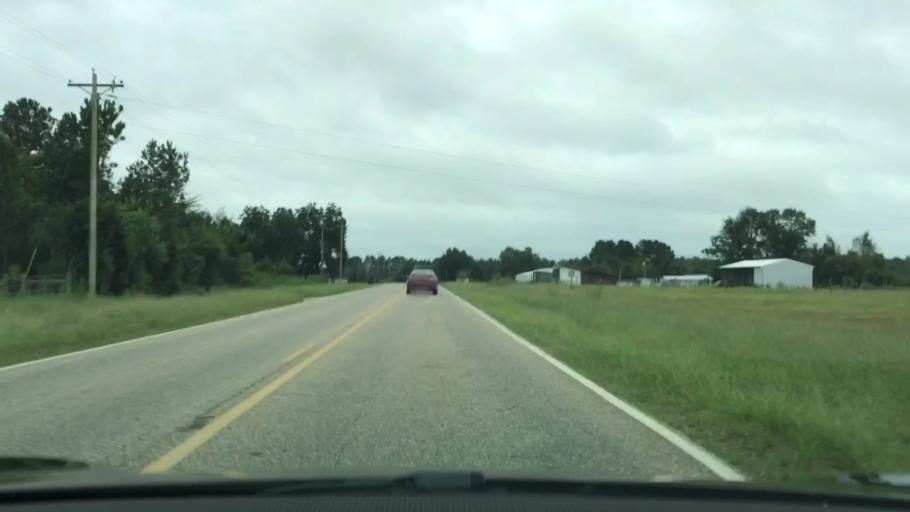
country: US
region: Alabama
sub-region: Geneva County
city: Samson
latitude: 31.1781
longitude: -86.1453
